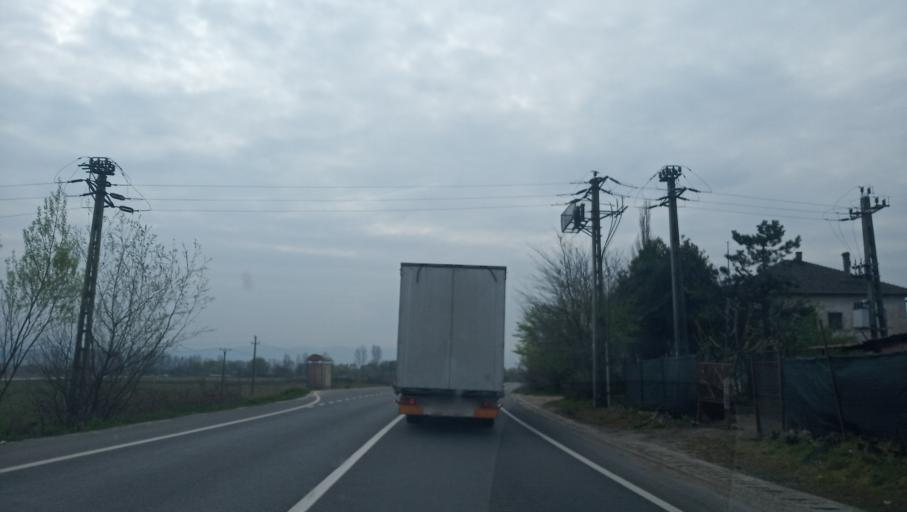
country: RO
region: Hunedoara
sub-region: Comuna Calan
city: Calan
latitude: 45.7599
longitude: 23.0008
